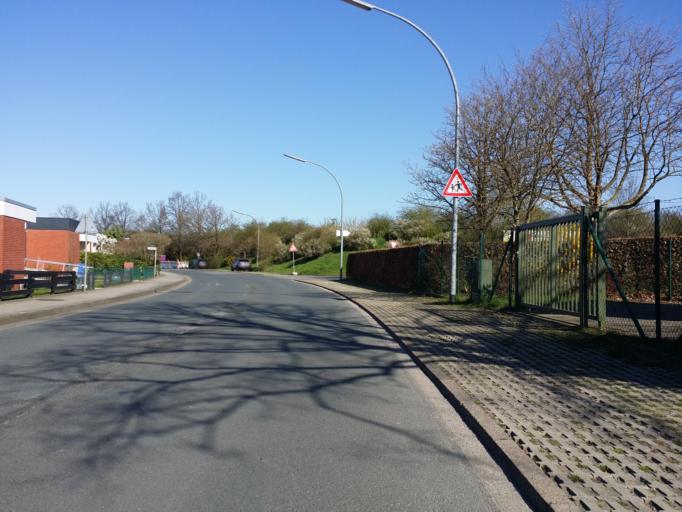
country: DE
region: Lower Saxony
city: Delmenhorst
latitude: 53.0275
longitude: 8.6611
